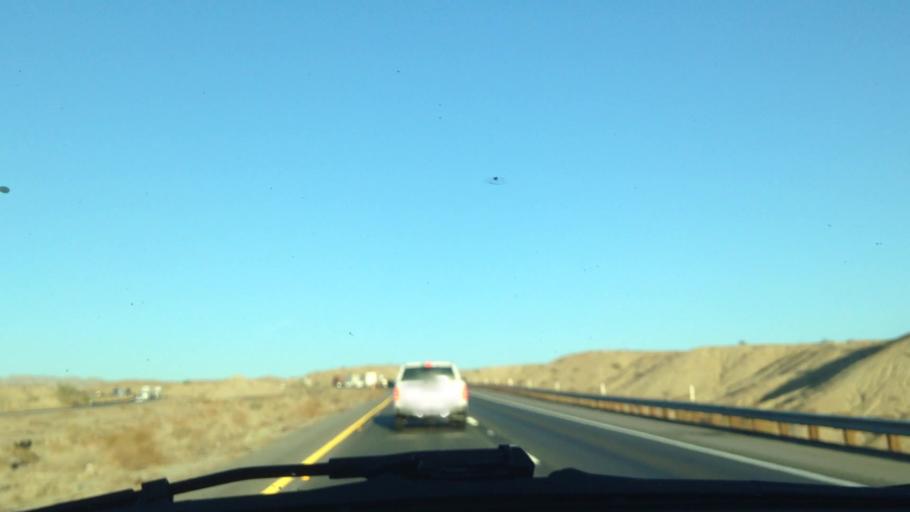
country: US
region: California
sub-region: Riverside County
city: Thermal
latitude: 33.6984
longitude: -116.1055
